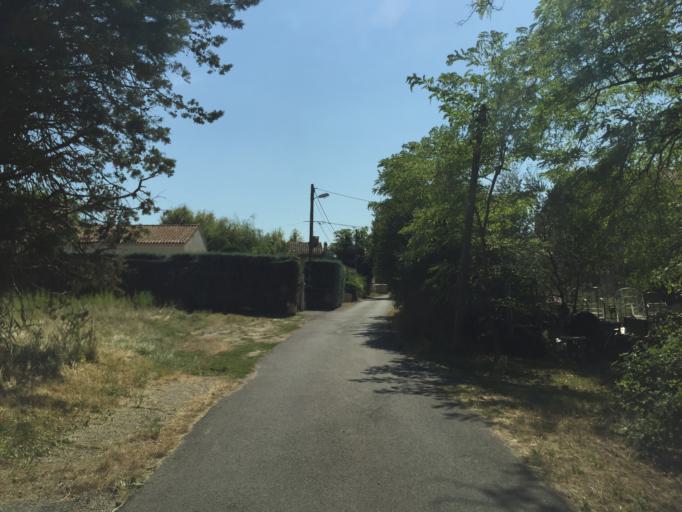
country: FR
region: Provence-Alpes-Cote d'Azur
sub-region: Departement du Vaucluse
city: Orange
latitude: 44.1004
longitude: 4.8167
